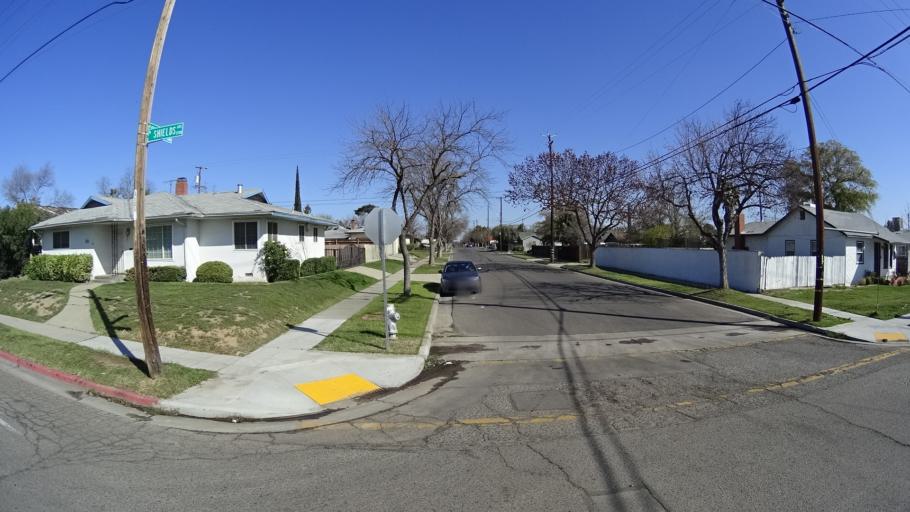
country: US
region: California
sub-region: Fresno County
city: Fresno
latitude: 36.7793
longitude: -119.8310
